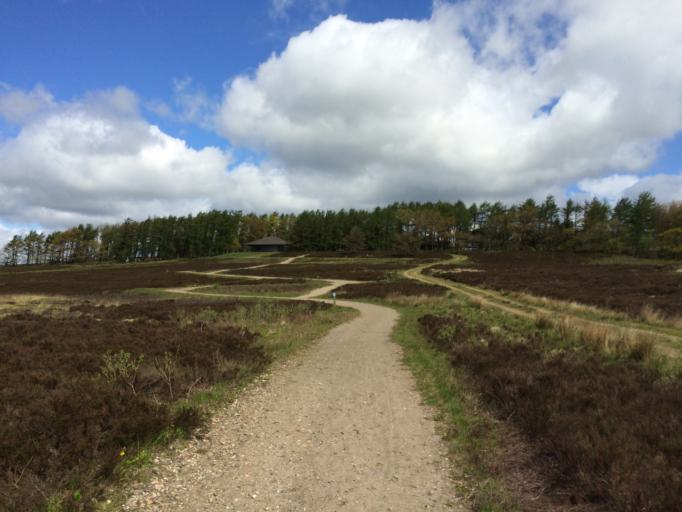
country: DK
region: Central Jutland
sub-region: Holstebro Kommune
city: Holstebro
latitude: 56.2286
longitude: 8.6206
